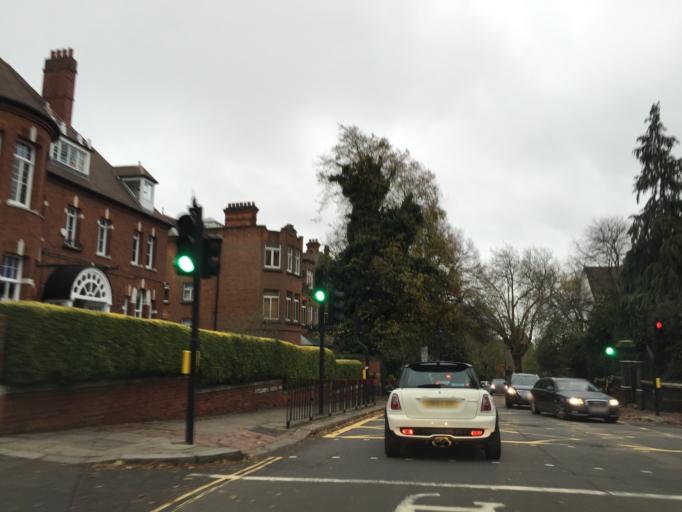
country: GB
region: England
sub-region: Greater London
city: Belsize Park
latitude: 51.5538
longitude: -0.1767
